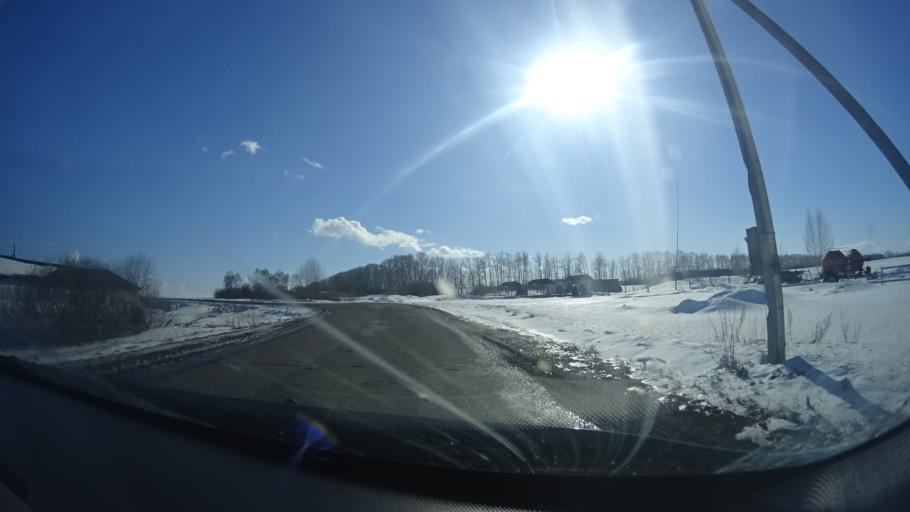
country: RU
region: Bashkortostan
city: Chishmy
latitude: 54.5900
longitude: 55.2573
